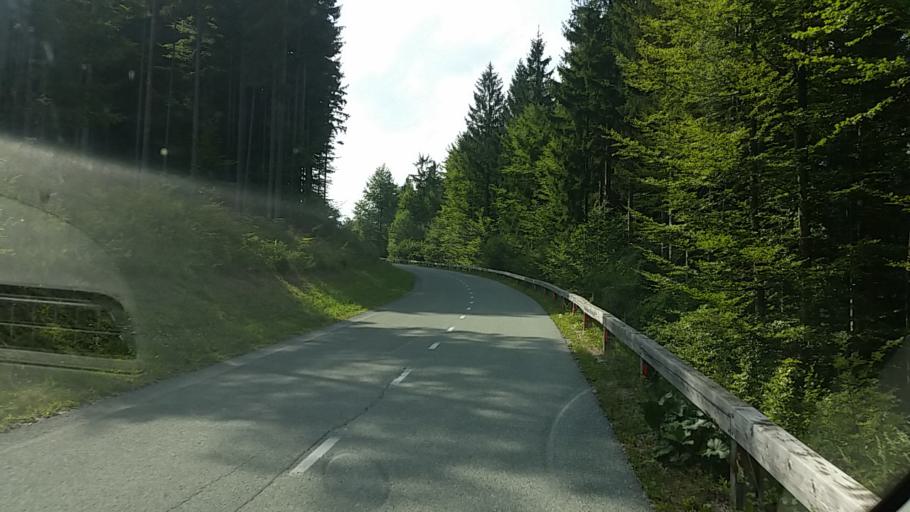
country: SI
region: Zelezniki
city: Zelezniki
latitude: 46.2126
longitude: 14.0445
